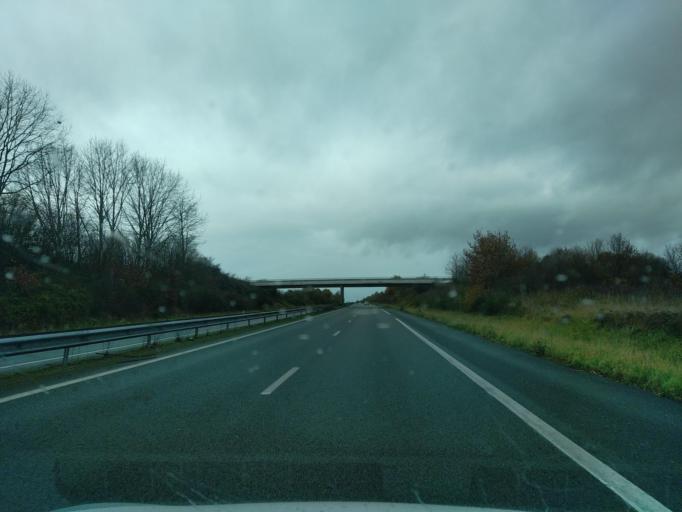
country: FR
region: Pays de la Loire
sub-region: Departement de la Vendee
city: Saint-Martin-des-Noyers
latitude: 46.7280
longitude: -1.1572
